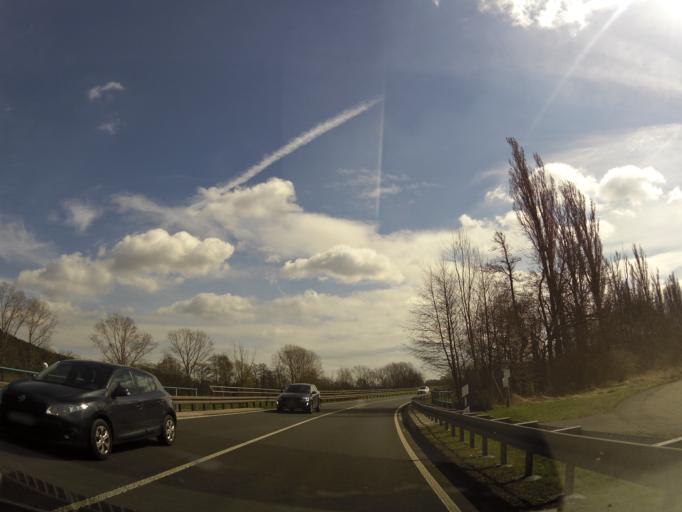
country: DE
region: Thuringia
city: Luisenthal
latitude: 50.8115
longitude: 10.7424
